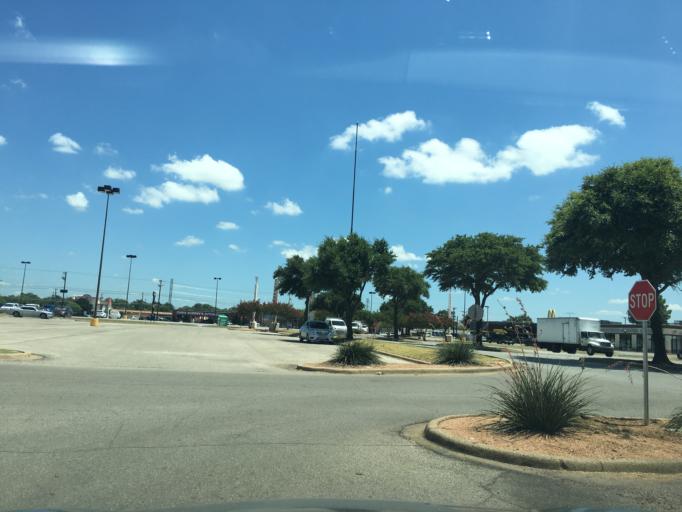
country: US
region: Texas
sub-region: Dallas County
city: Garland
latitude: 32.8498
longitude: -96.6856
